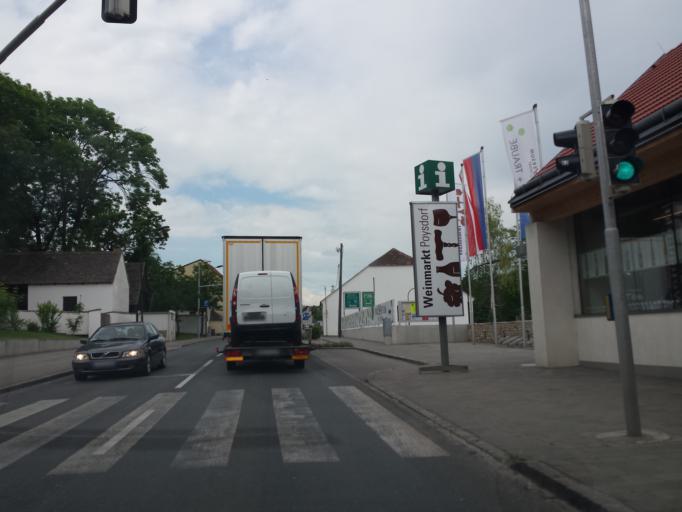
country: AT
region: Lower Austria
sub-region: Politischer Bezirk Mistelbach
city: Poysdorf
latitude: 48.6715
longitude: 16.6294
